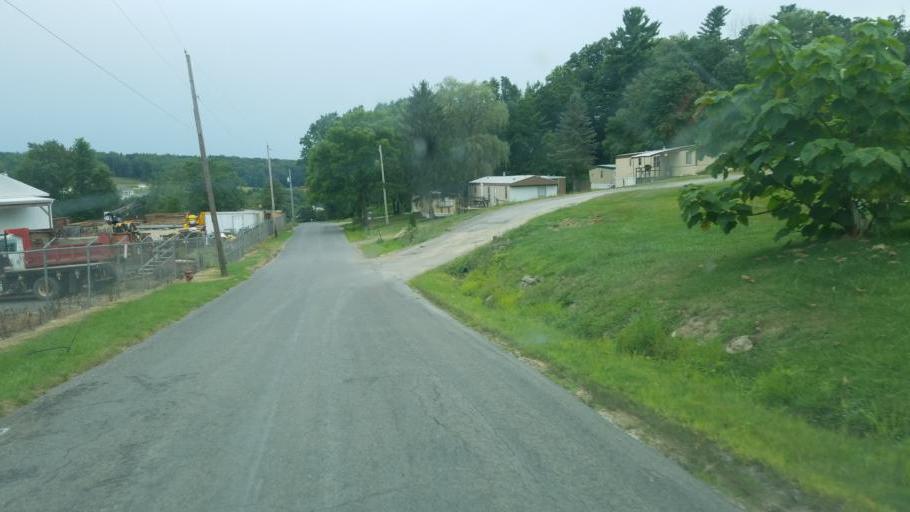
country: US
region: Pennsylvania
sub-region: Clarion County
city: Clarion
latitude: 41.2080
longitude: -79.3925
